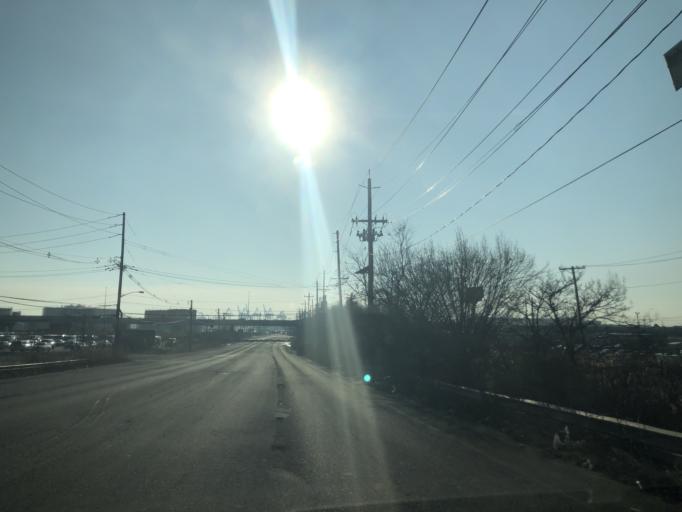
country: US
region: New Jersey
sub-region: Hudson County
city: Bayonne
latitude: 40.7033
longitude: -74.1362
